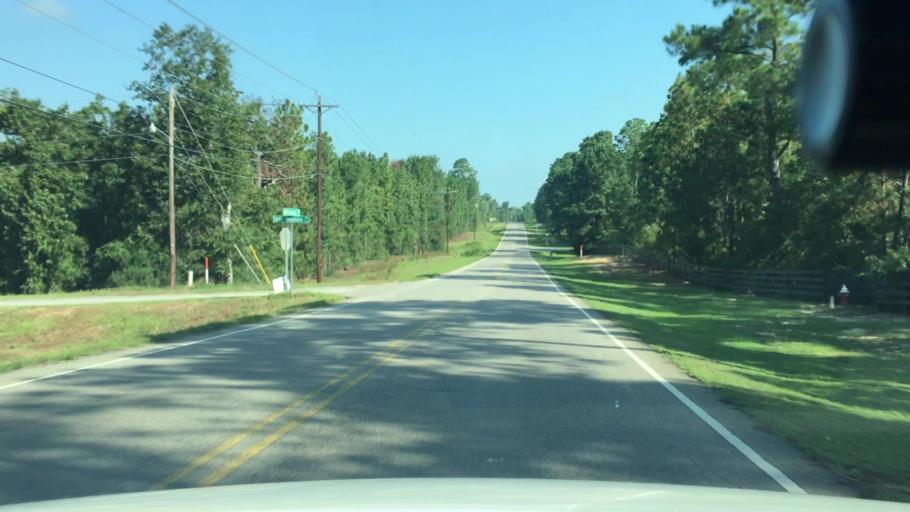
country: US
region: South Carolina
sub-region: Aiken County
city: Graniteville
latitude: 33.5957
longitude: -81.8387
